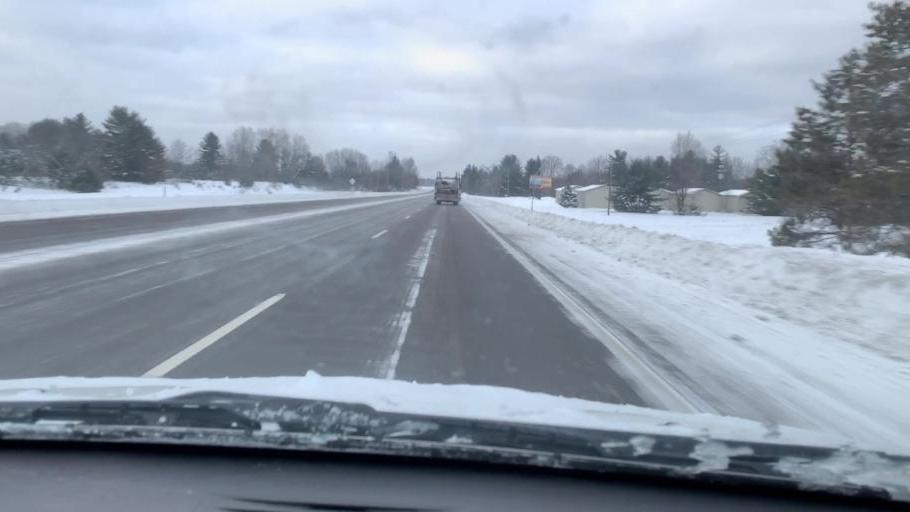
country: US
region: Michigan
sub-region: Kalkaska County
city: Kalkaska
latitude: 44.6797
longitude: -85.2291
